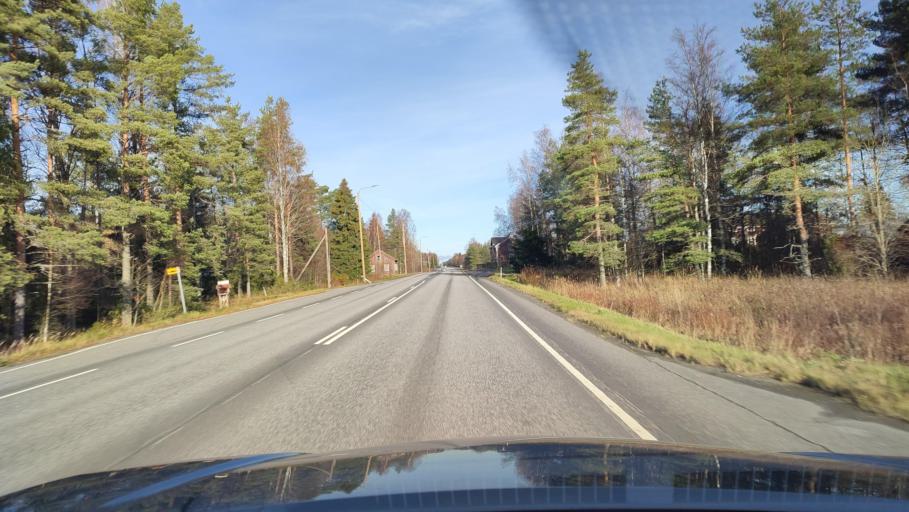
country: FI
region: Ostrobothnia
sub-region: Vaasa
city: Malax
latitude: 62.7709
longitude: 21.6578
